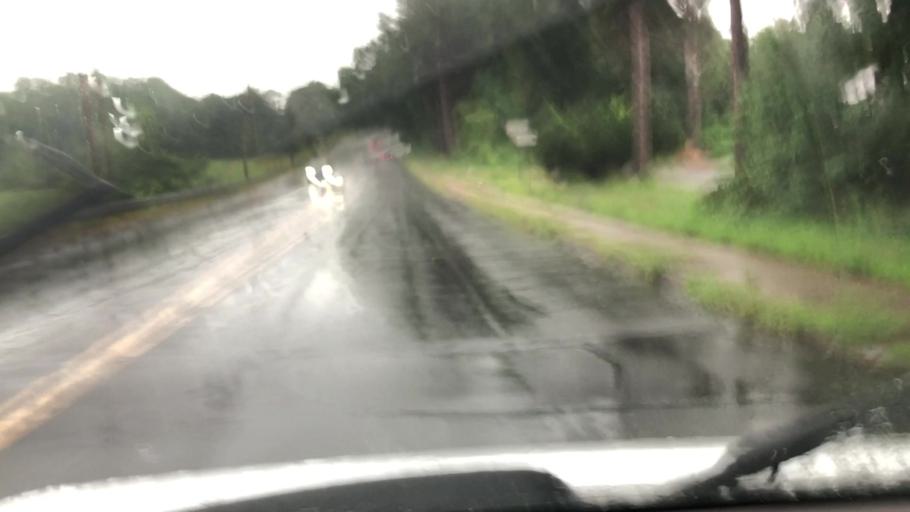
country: US
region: Massachusetts
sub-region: Hampshire County
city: Northampton
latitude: 42.3333
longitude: -72.6588
